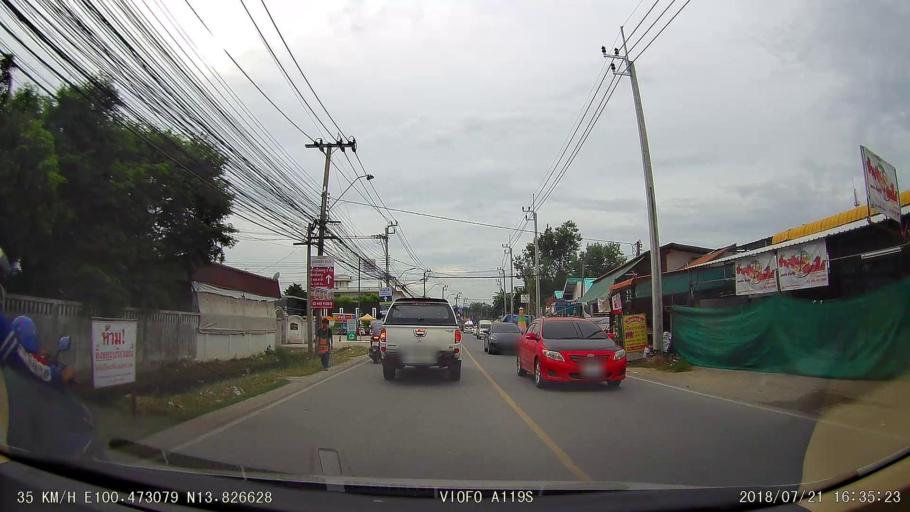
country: TH
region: Nonthaburi
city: Bang Kruai
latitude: 13.8266
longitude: 100.4731
